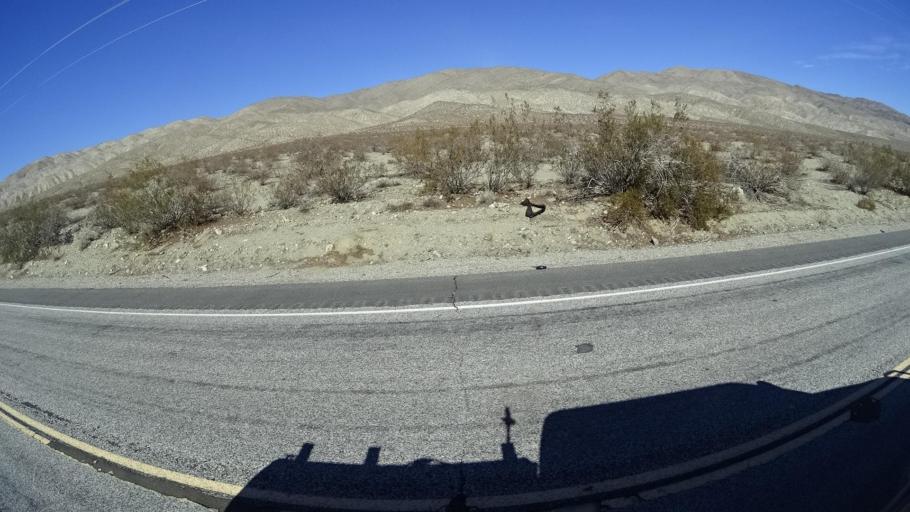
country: US
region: California
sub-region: Kern County
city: Inyokern
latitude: 35.3769
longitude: -117.8638
